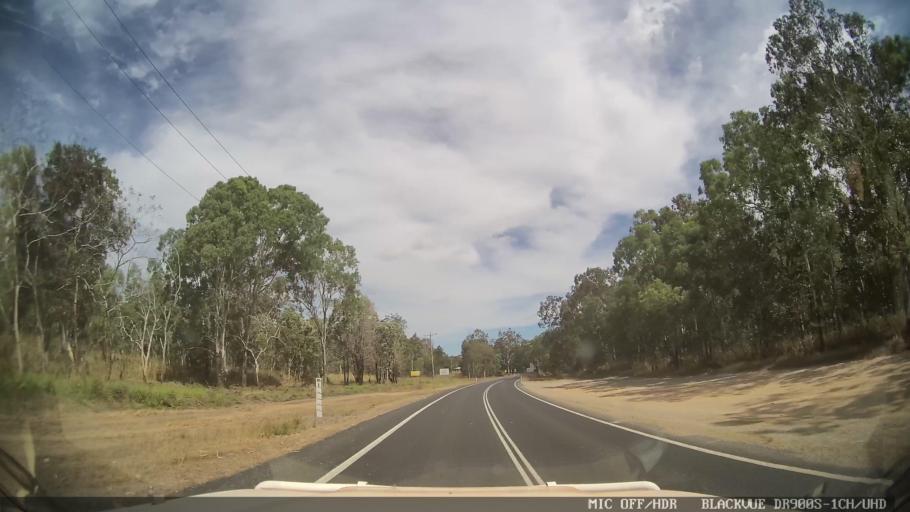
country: AU
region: Queensland
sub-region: Cairns
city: Port Douglas
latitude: -16.6682
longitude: 145.3291
